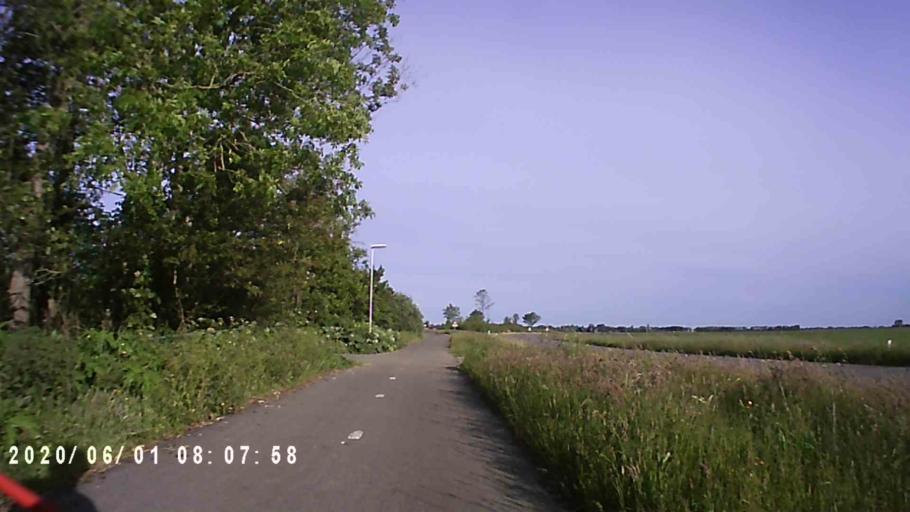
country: NL
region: Friesland
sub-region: Gemeente Ferwerderadiel
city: Burdaard
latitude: 53.2832
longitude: 5.9008
